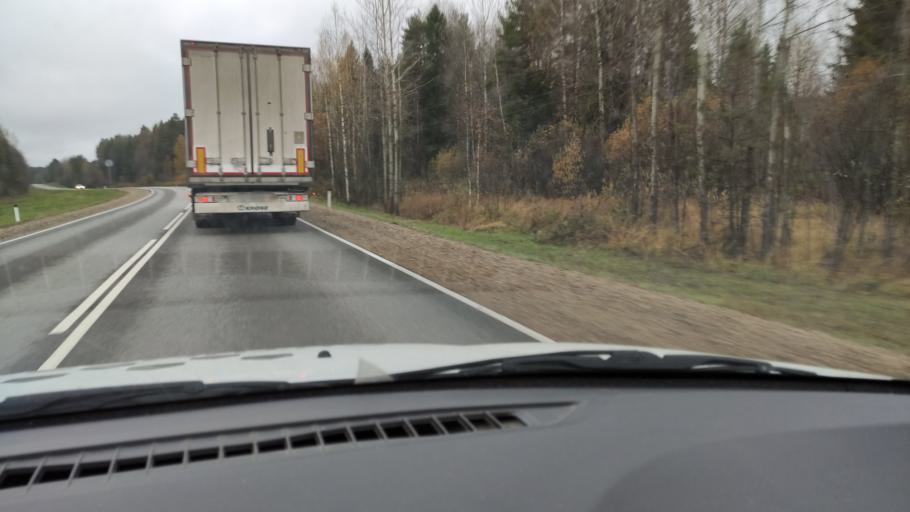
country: RU
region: Kirov
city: Slobodskoy
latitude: 58.7743
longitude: 50.3806
